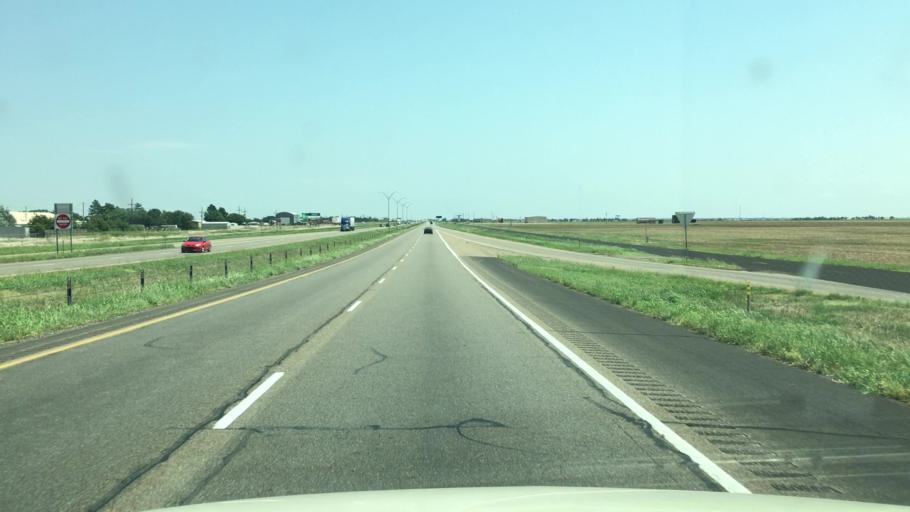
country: US
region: Texas
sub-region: Potter County
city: Bushland
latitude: 35.1899
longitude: -102.0069
